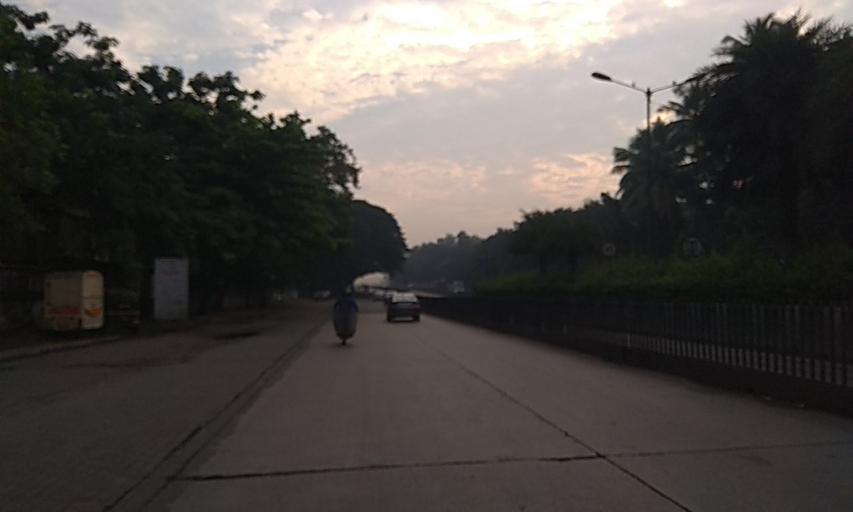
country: IN
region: Maharashtra
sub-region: Pune Division
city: Khadki
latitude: 18.5528
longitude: 73.8981
